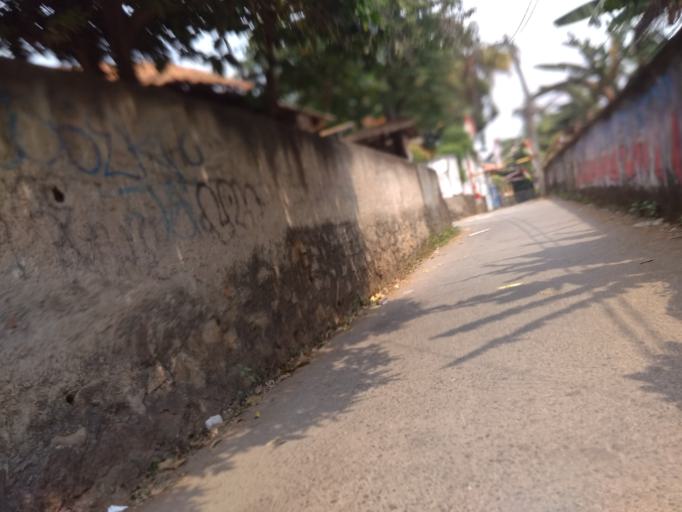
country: ID
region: West Java
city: Pamulang
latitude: -6.3217
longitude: 106.7912
